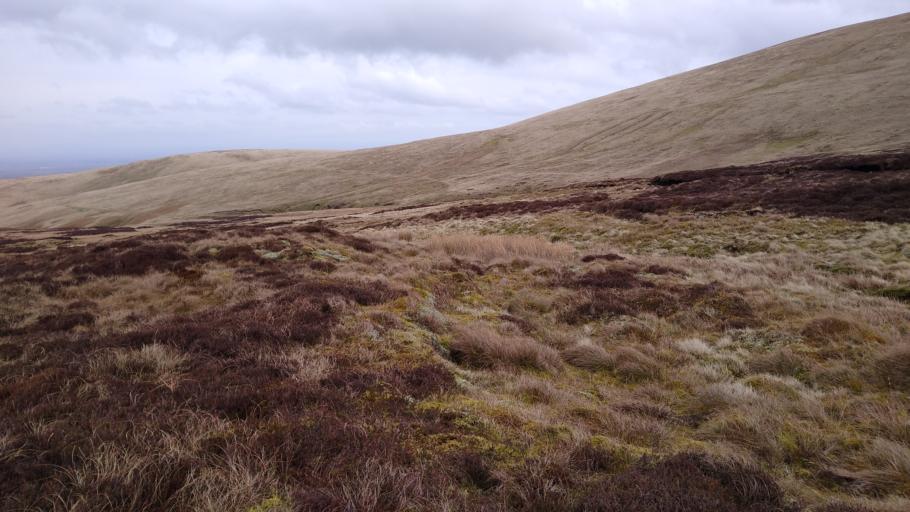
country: GB
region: England
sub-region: Cumbria
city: Keswick
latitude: 54.7038
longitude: -3.0718
